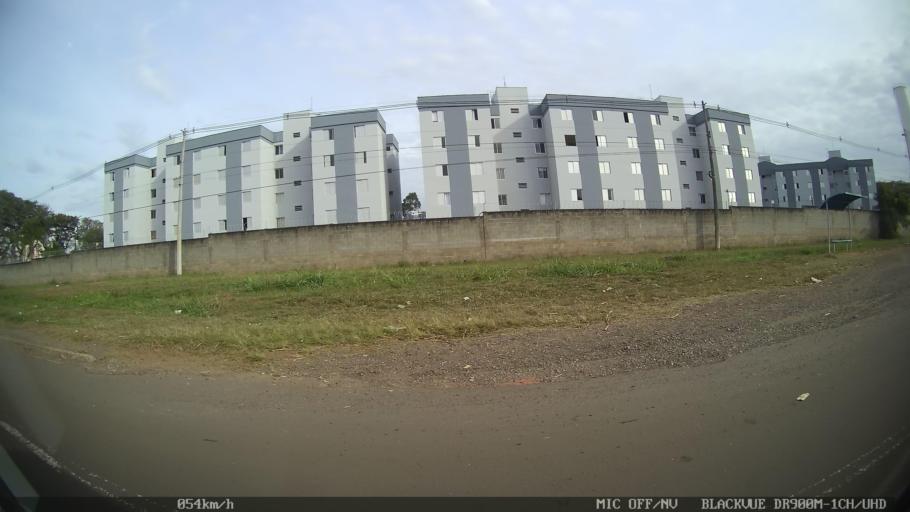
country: BR
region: Sao Paulo
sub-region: Piracicaba
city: Piracicaba
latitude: -22.7386
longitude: -47.5917
